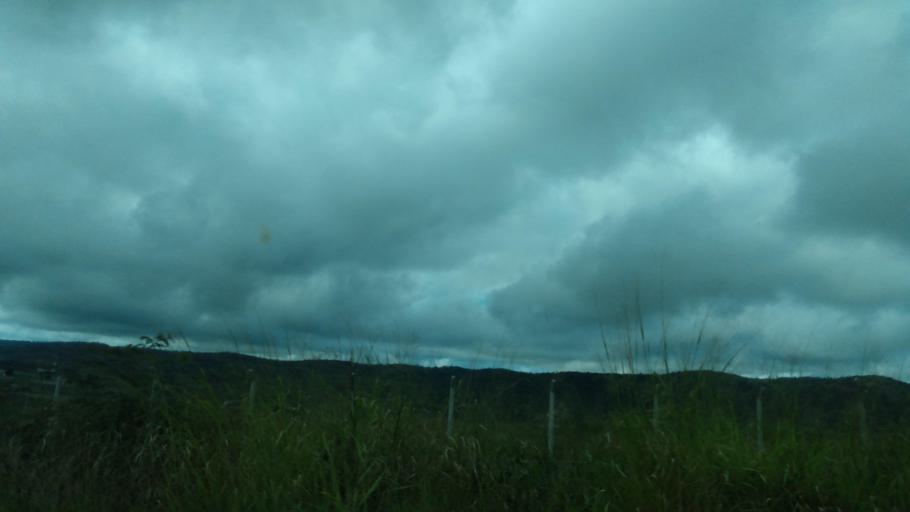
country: BR
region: Pernambuco
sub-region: Caruaru
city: Caruaru
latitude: -8.3162
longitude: -35.9767
